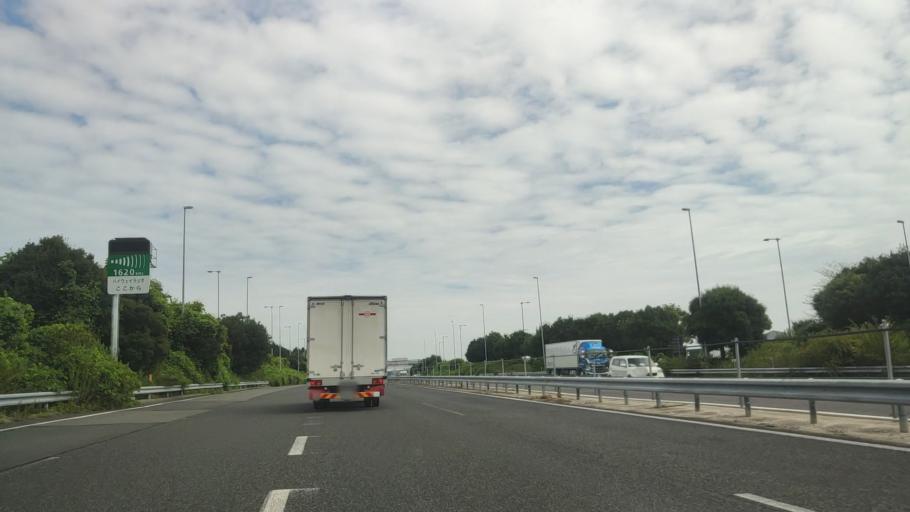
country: JP
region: Mie
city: Kameyama
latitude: 34.8660
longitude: 136.4141
